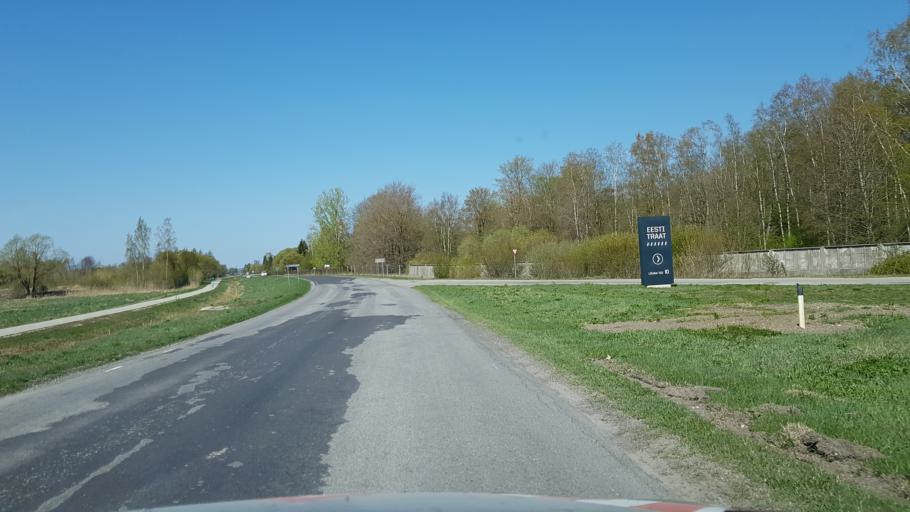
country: EE
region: Harju
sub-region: Joelaehtme vald
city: Loo
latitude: 59.4273
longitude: 24.9446
